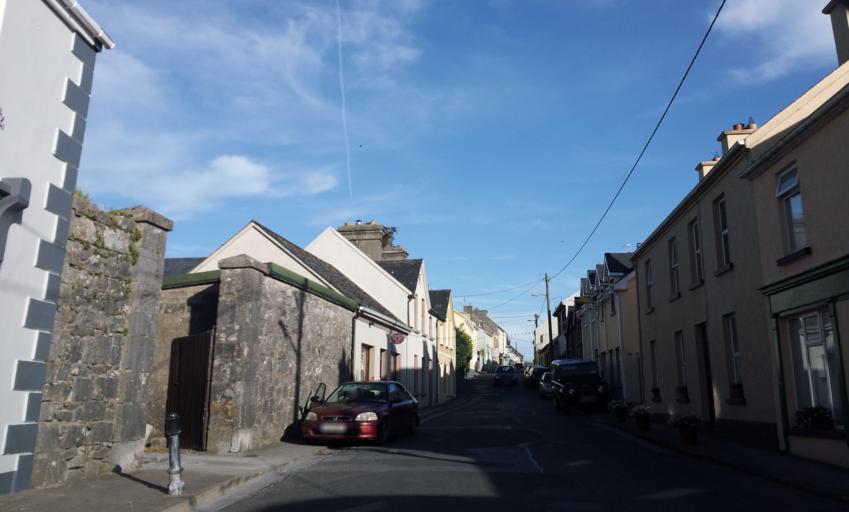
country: IE
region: Munster
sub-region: An Clar
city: Ennis
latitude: 52.9459
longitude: -9.0666
